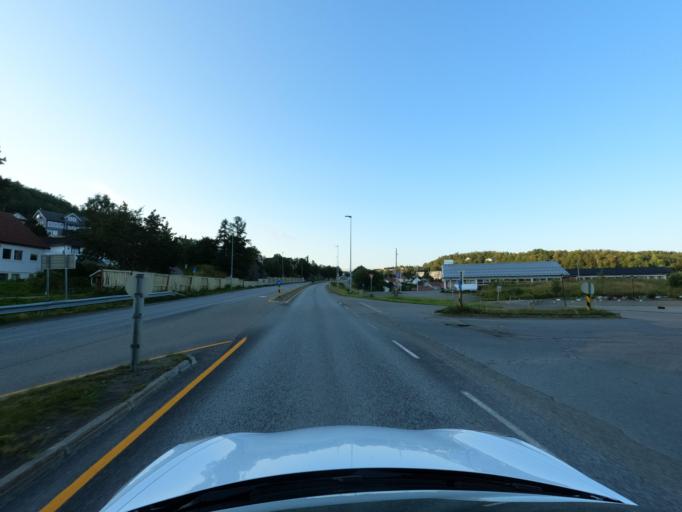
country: NO
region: Troms
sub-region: Harstad
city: Harstad
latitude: 68.7731
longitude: 16.5593
